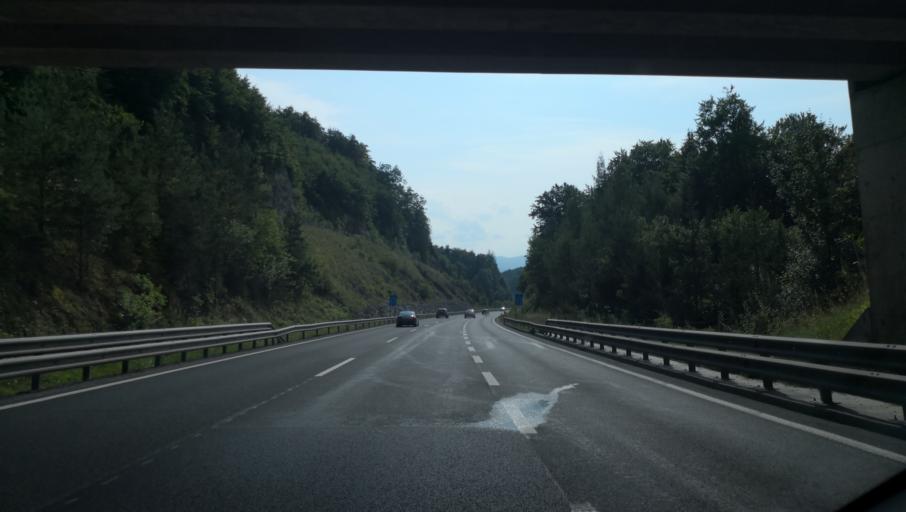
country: SI
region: Grosuplje
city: Grosuplje
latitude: 45.9775
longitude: 14.6846
